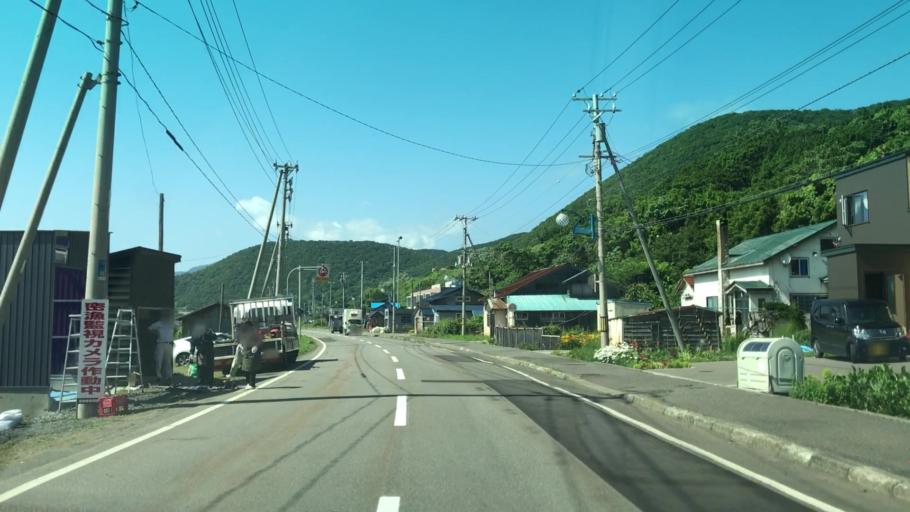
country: JP
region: Hokkaido
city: Iwanai
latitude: 43.0947
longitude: 140.4634
